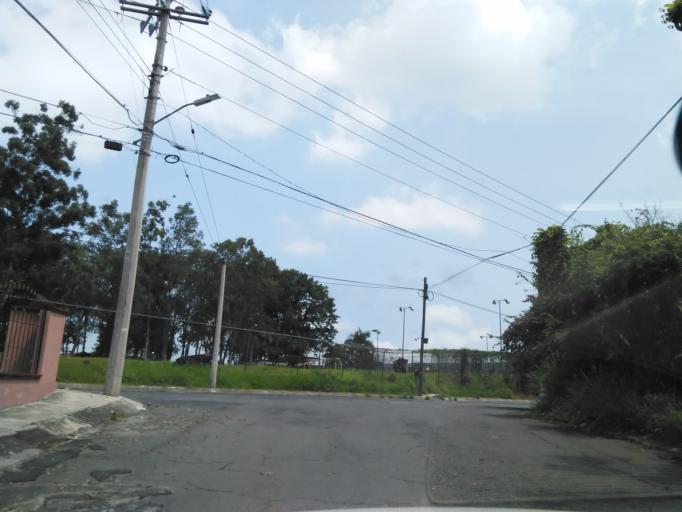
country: MX
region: Nayarit
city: Tepic
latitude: 21.5143
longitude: -104.9210
